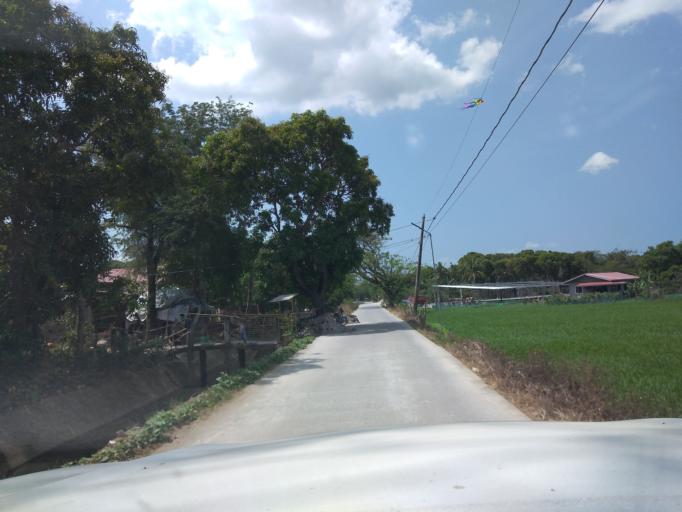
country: PH
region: Central Luzon
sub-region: Province of Pampanga
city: Bahay Pare
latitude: 15.0338
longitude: 120.8761
